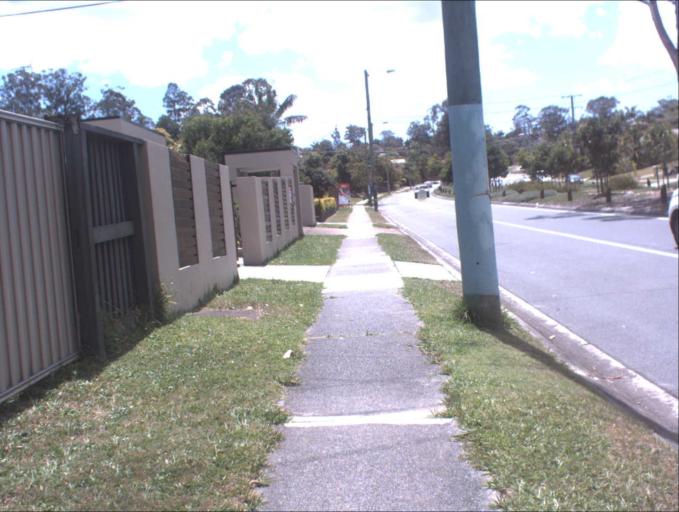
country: AU
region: Queensland
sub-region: Logan
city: Slacks Creek
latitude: -27.6543
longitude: 153.1717
